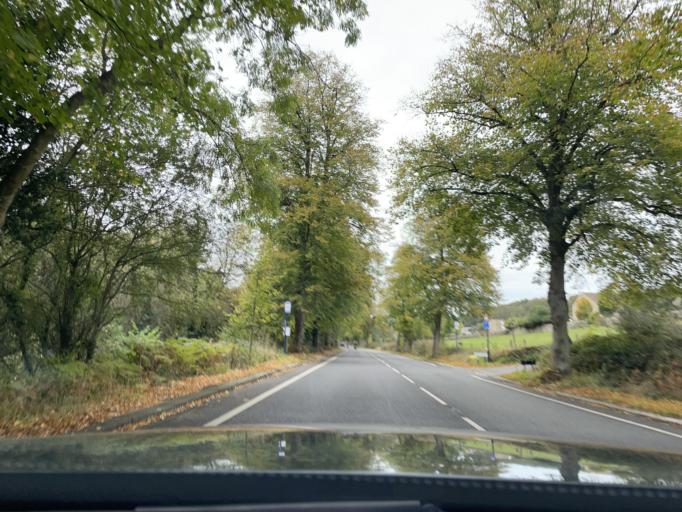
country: GB
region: England
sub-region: Sheffield
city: Oughtibridge
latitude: 53.3847
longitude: -1.5384
